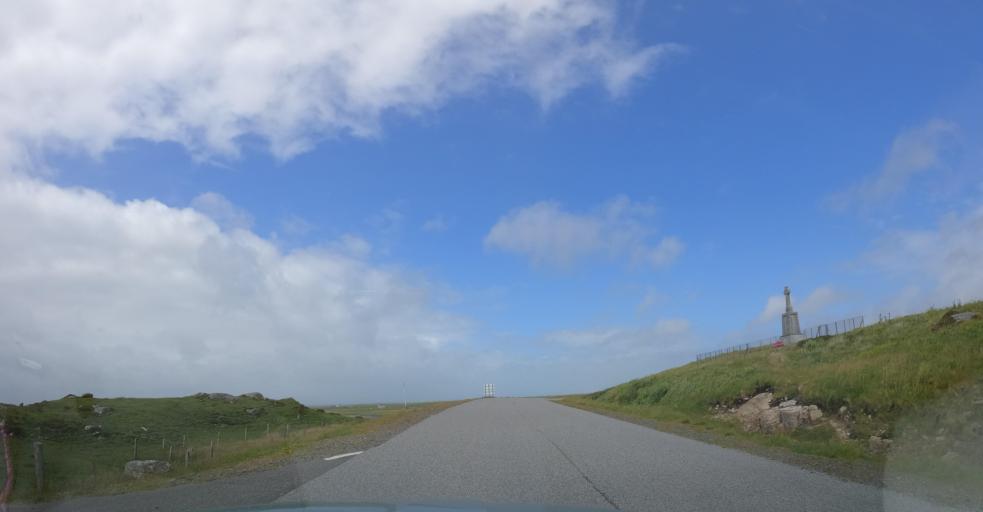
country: GB
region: Scotland
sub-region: Eilean Siar
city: Isle of South Uist
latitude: 57.2319
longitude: -7.3978
